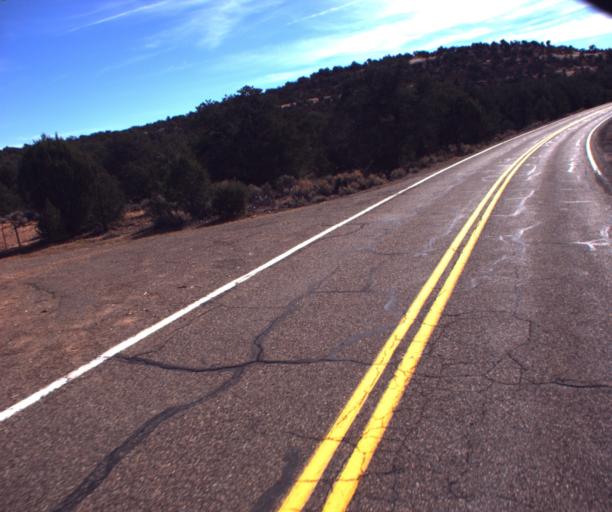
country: US
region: Arizona
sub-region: Navajo County
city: Kayenta
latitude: 36.6545
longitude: -110.5195
